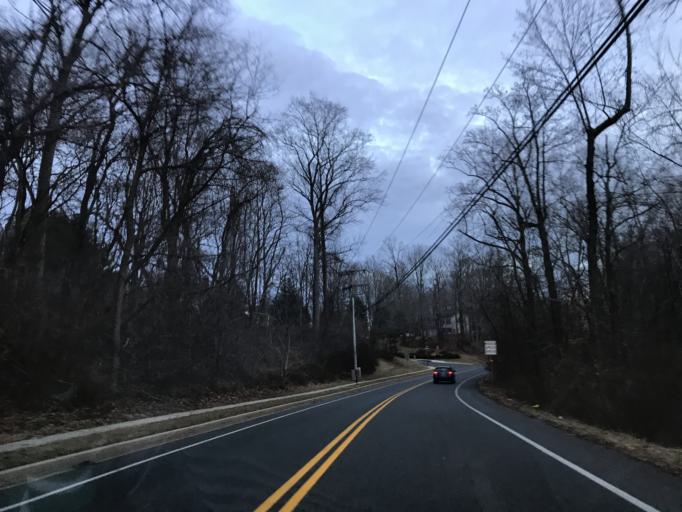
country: US
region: Maryland
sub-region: Harford County
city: Bel Air South
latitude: 39.4866
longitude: -76.3031
